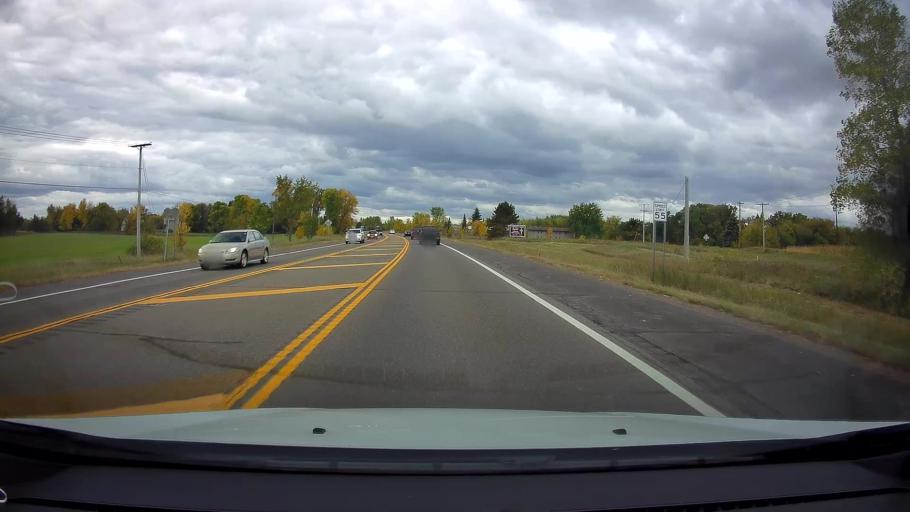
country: US
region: Minnesota
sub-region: Chisago County
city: Chisago City
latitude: 45.3547
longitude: -92.9110
